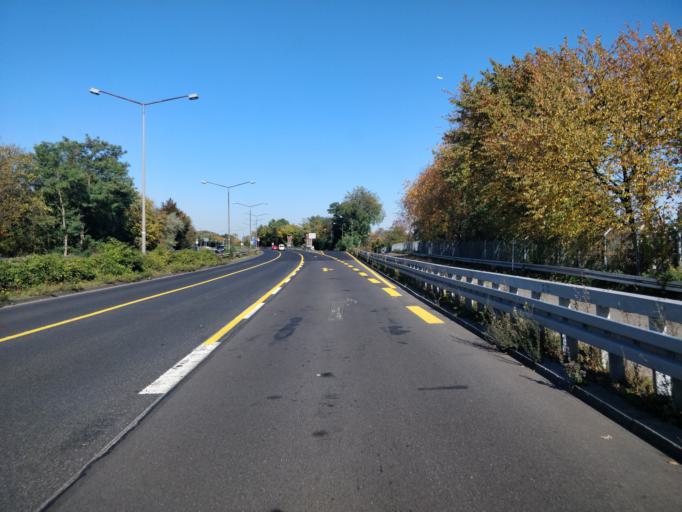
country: DE
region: North Rhine-Westphalia
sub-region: Regierungsbezirk Koln
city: Leverkusen
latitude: 51.0182
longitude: 6.9474
